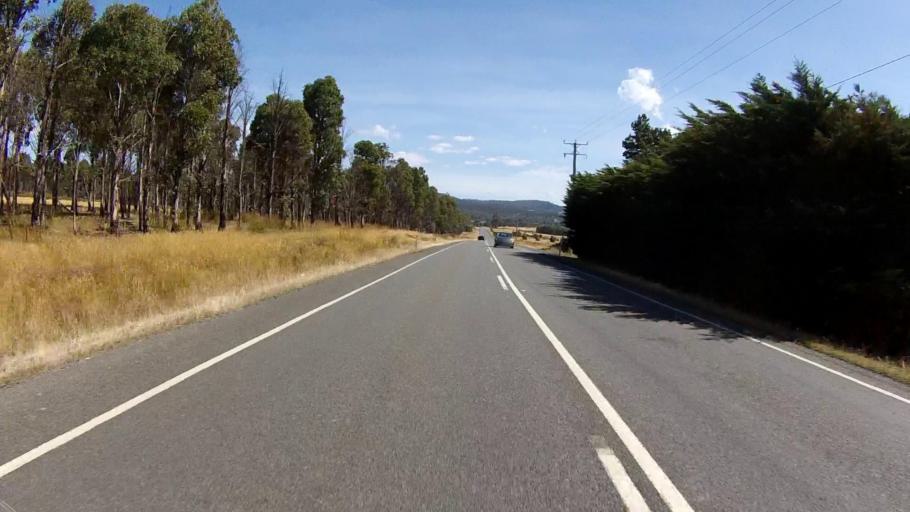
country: AU
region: Tasmania
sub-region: Sorell
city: Sorell
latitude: -42.6040
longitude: 147.7494
